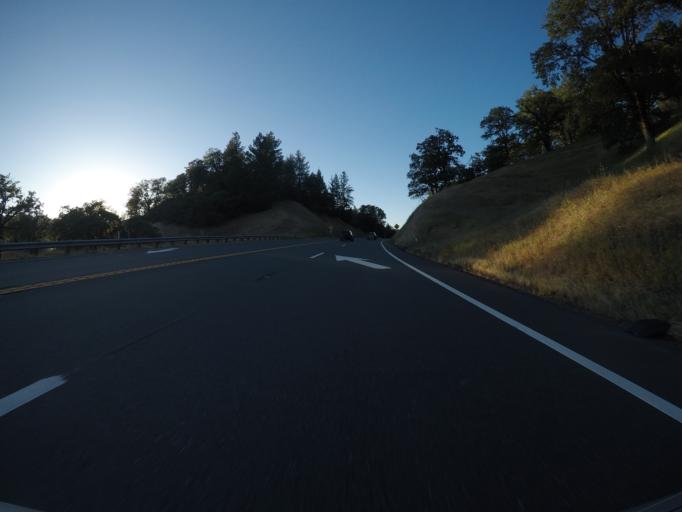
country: US
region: California
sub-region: Mendocino County
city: Laytonville
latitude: 39.7540
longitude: -123.5366
